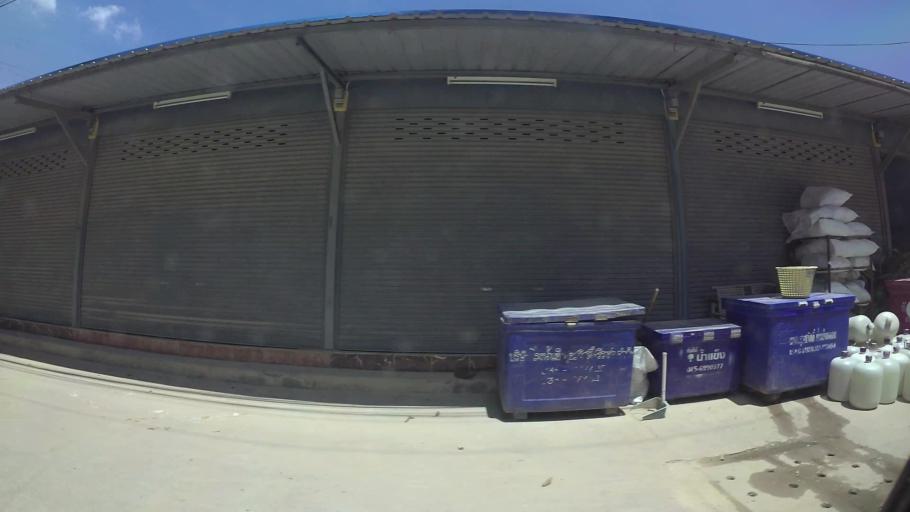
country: TH
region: Chon Buri
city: Si Racha
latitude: 13.1294
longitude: 100.9533
